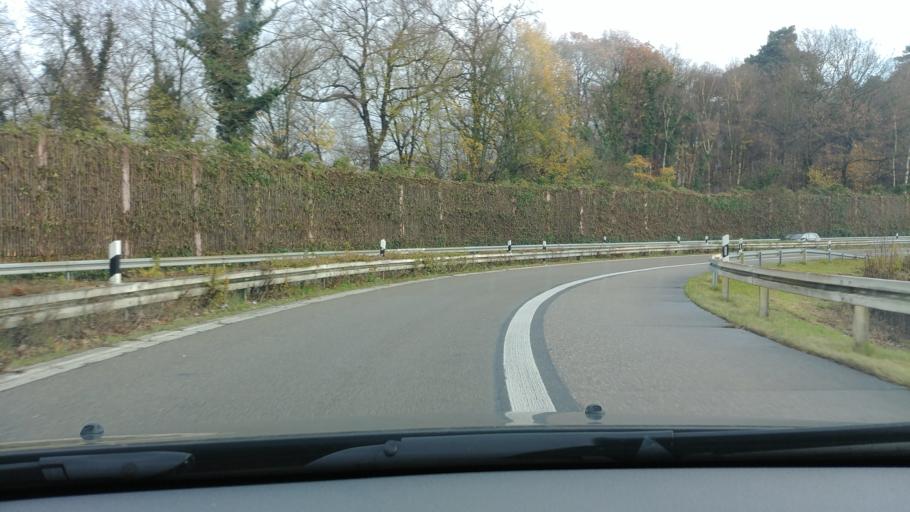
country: DE
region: North Rhine-Westphalia
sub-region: Regierungsbezirk Koln
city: Bergisch Gladbach
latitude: 50.9511
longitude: 7.1264
